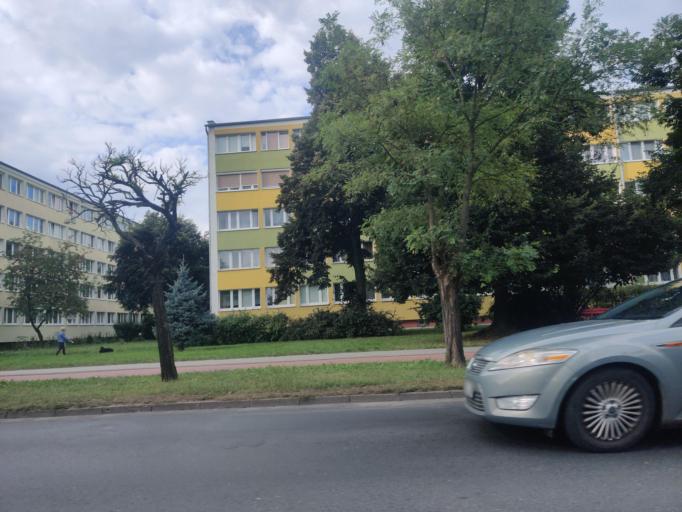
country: PL
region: Greater Poland Voivodeship
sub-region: Konin
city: Konin
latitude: 52.2273
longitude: 18.2678
